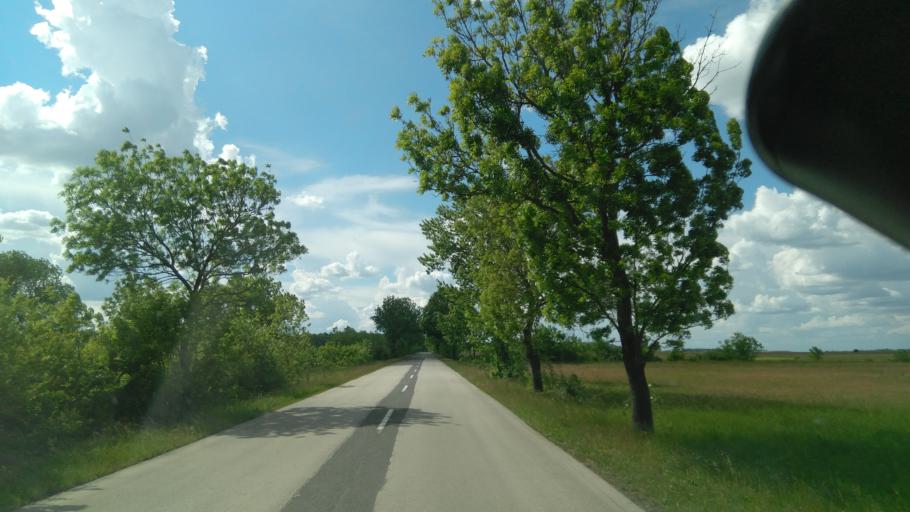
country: HU
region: Bekes
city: Bucsa
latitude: 47.1779
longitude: 21.0562
